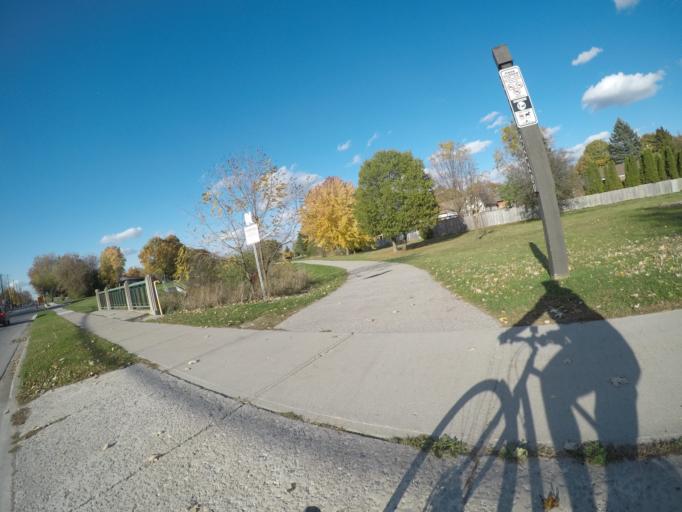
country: CA
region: Ontario
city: Kitchener
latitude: 43.4241
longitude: -80.4592
